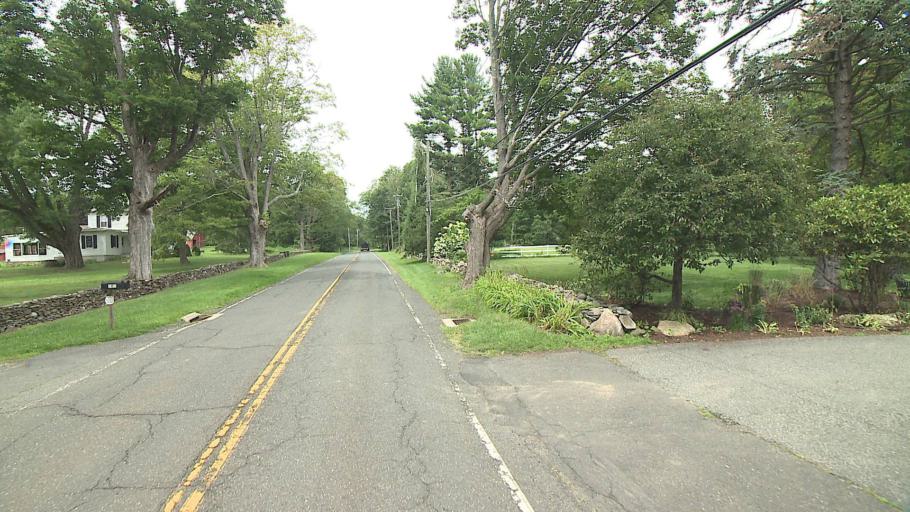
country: US
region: Connecticut
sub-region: Litchfield County
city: New Milford
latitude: 41.5231
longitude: -73.3641
